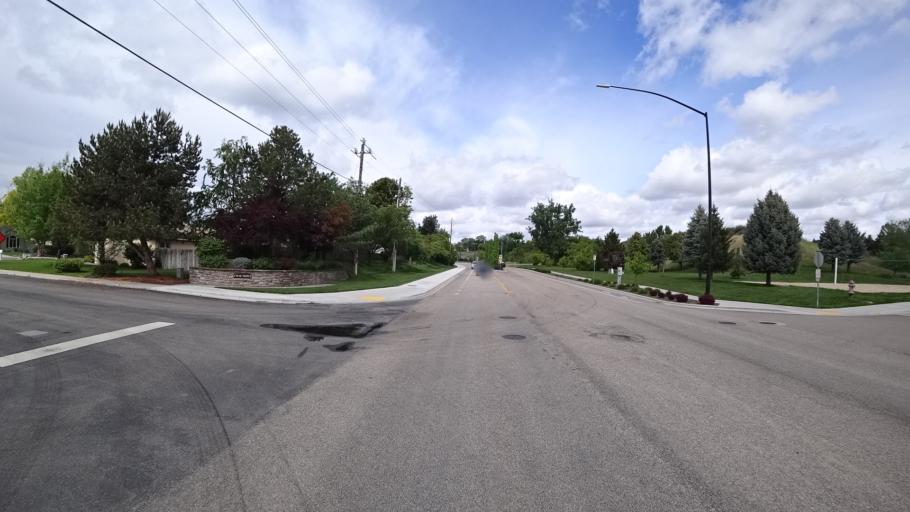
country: US
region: Idaho
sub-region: Ada County
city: Eagle
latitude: 43.6950
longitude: -116.3259
